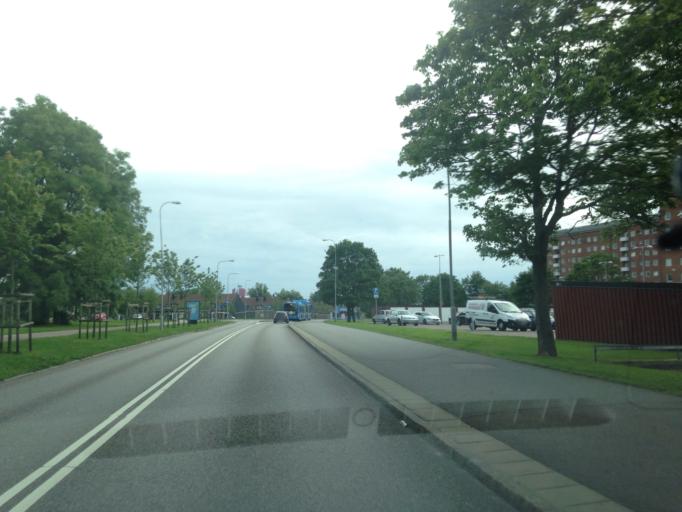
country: SE
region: Vaestra Goetaland
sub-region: Goteborg
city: Goeteborg
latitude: 57.7299
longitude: 11.9746
